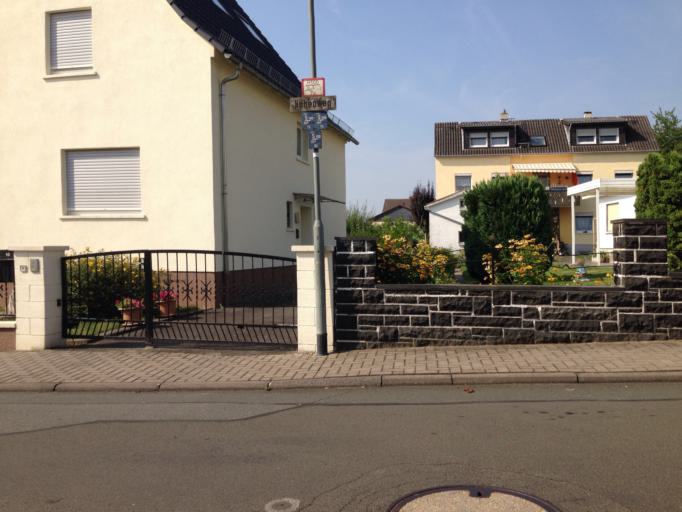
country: DE
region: Hesse
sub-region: Regierungsbezirk Giessen
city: Giessen
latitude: 50.6042
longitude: 8.6947
